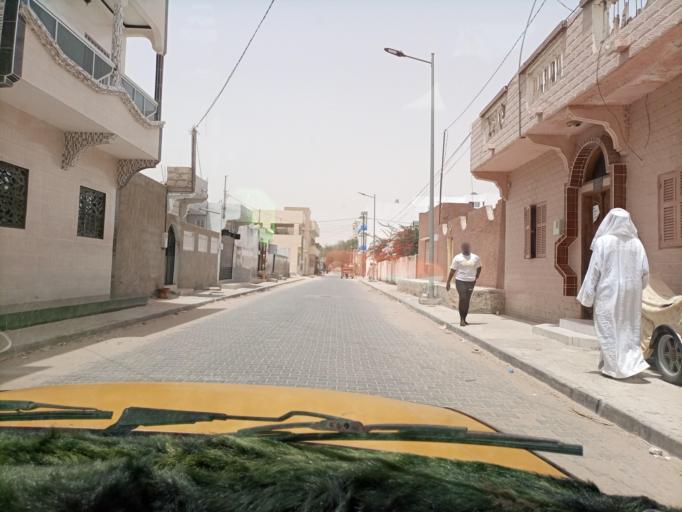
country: SN
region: Saint-Louis
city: Saint-Louis
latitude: 16.0222
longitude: -16.4892
